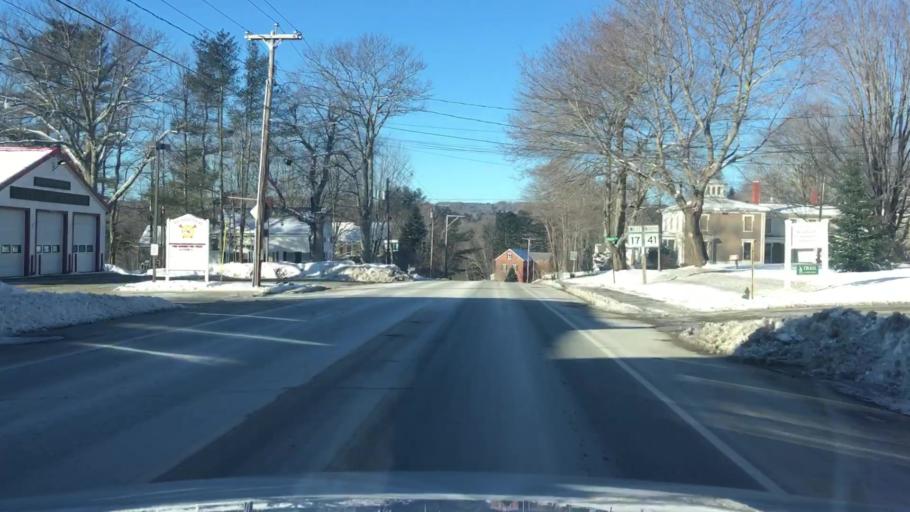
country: US
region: Maine
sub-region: Kennebec County
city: Readfield
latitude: 44.3880
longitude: -69.9670
